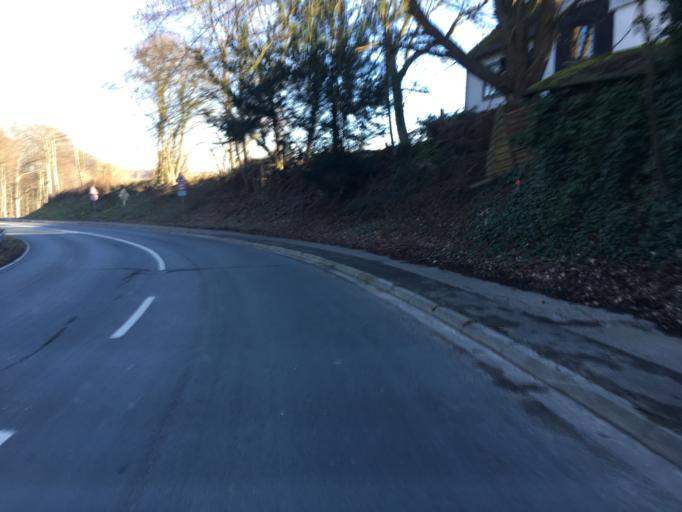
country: DE
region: North Rhine-Westphalia
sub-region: Regierungsbezirk Koln
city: Odenthal
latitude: 51.0587
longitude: 7.1239
